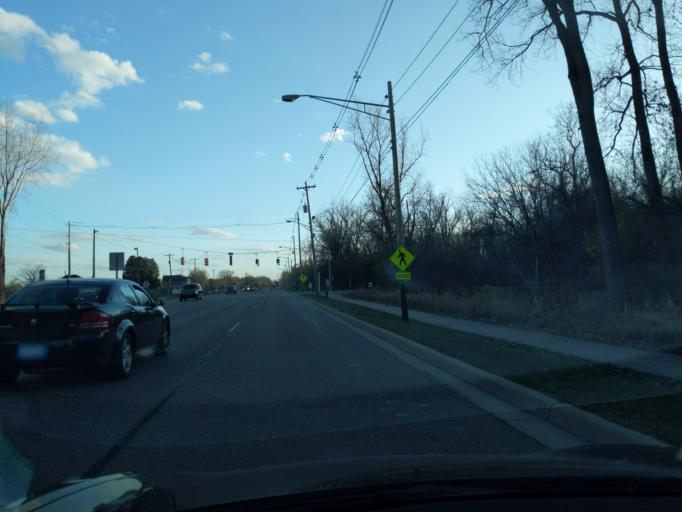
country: US
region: Michigan
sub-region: Ingham County
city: East Lansing
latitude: 42.7673
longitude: -84.4837
